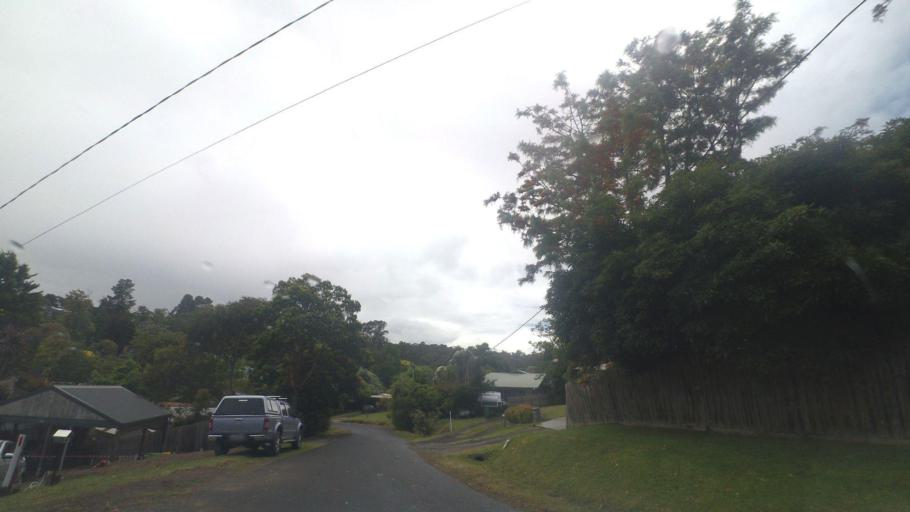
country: AU
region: Victoria
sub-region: Yarra Ranges
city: Mount Evelyn
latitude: -37.7674
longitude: 145.3689
